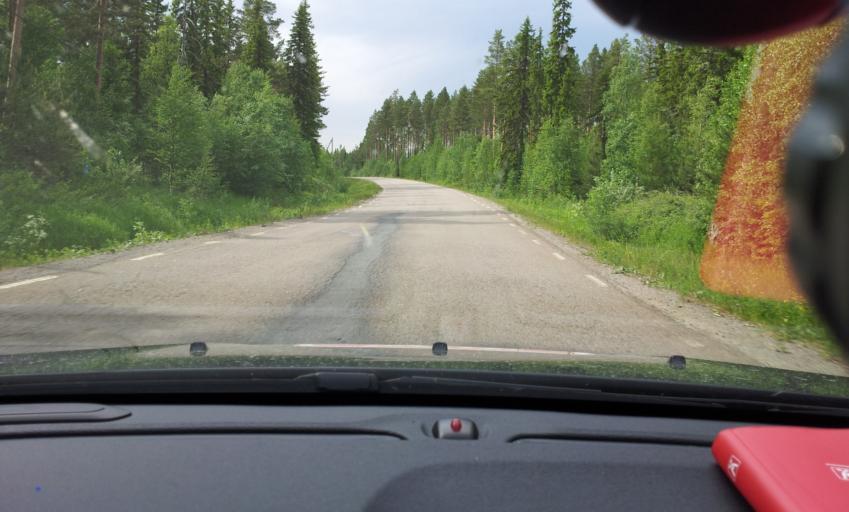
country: SE
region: Jaemtland
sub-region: Bergs Kommun
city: Hoverberg
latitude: 62.6601
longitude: 14.7799
